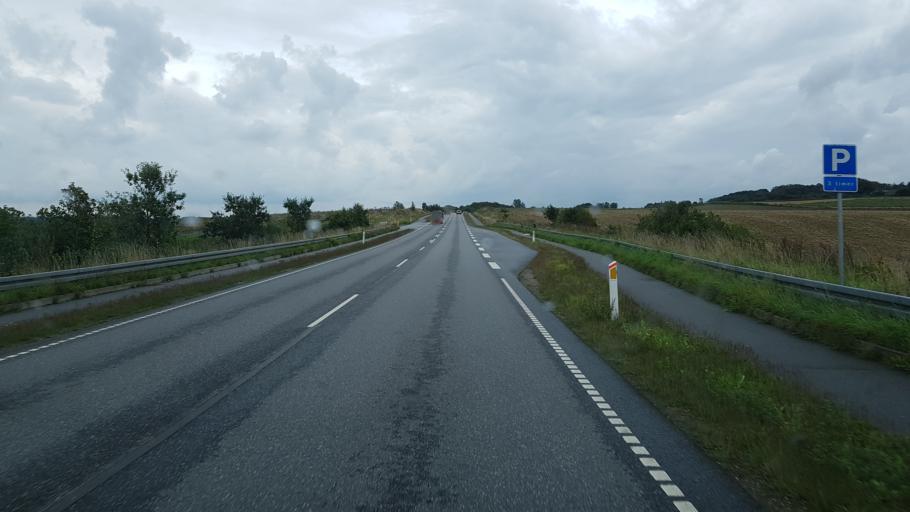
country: DK
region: Central Jutland
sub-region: Horsens Kommune
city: Horsens
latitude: 55.9052
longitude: 9.7375
